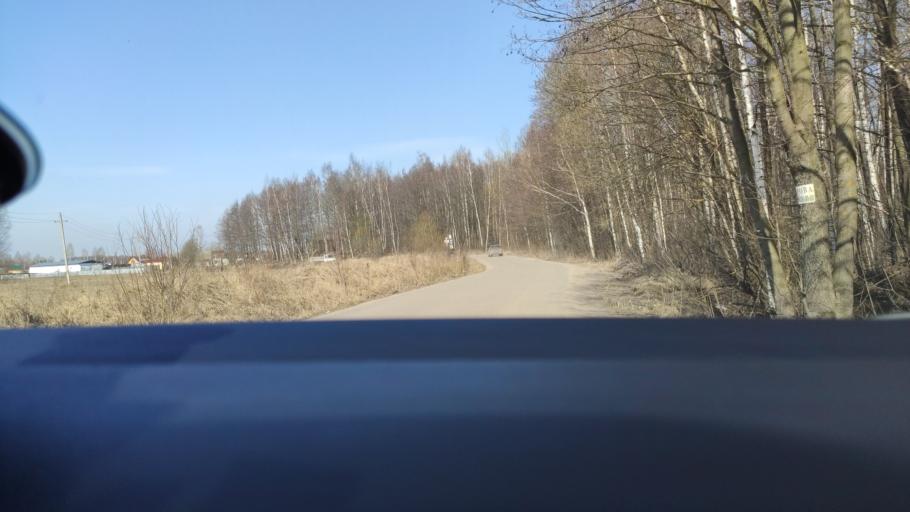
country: RU
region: Moskovskaya
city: Imeni Vorovskogo
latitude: 55.7753
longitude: 38.3767
